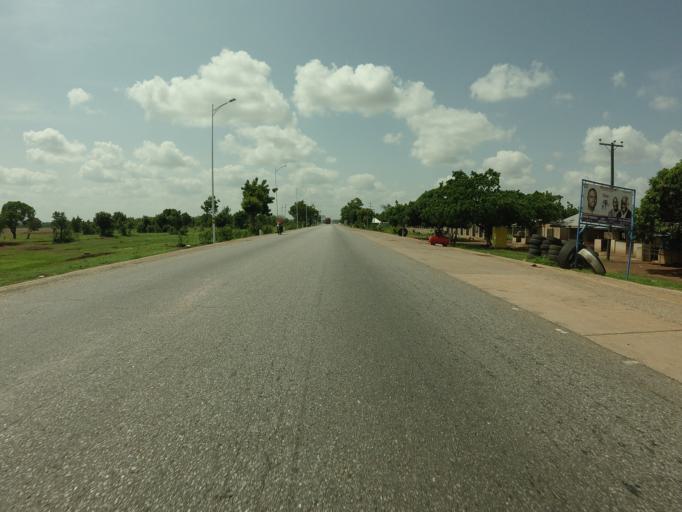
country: GH
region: Northern
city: Savelugu
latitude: 9.5467
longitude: -0.8382
